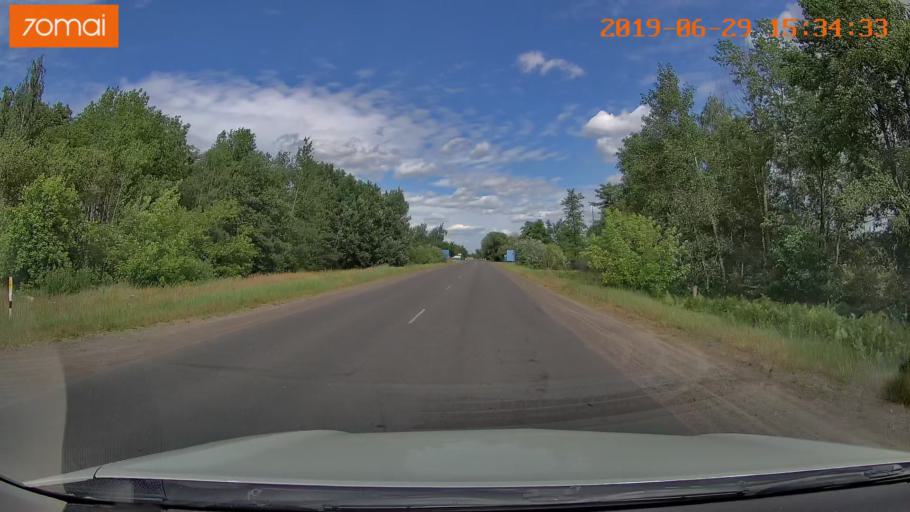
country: BY
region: Brest
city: Mikashevichy
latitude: 52.2141
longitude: 27.4584
